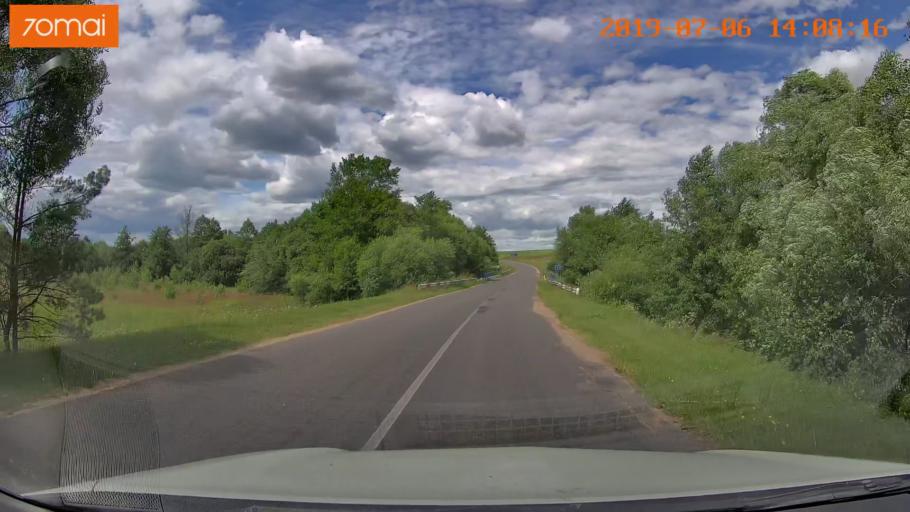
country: BY
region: Minsk
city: Ivyanyets
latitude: 53.8734
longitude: 26.7591
